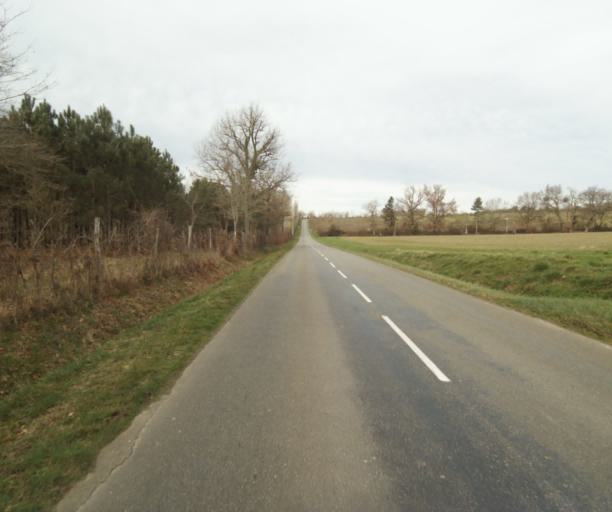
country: FR
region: Aquitaine
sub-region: Departement des Landes
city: Gabarret
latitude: 43.9596
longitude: 0.0065
